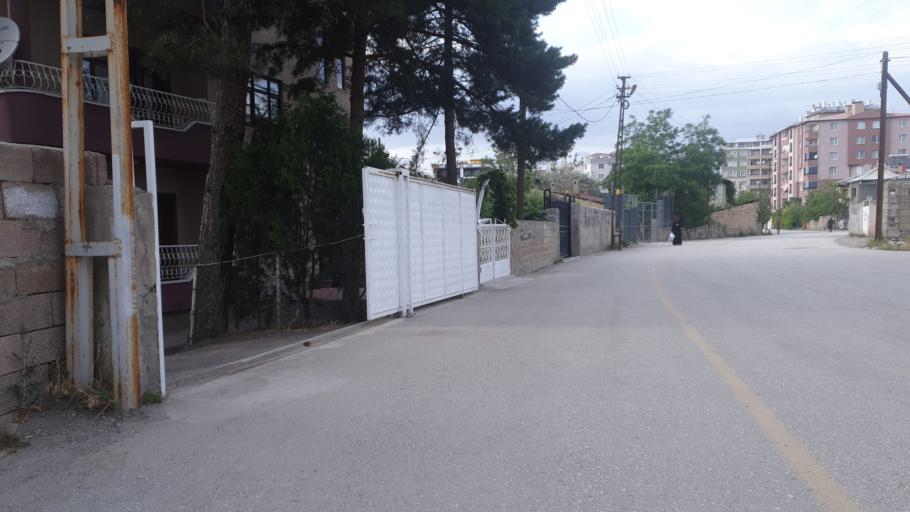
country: TR
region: Van
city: Van
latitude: 38.4898
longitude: 43.3892
